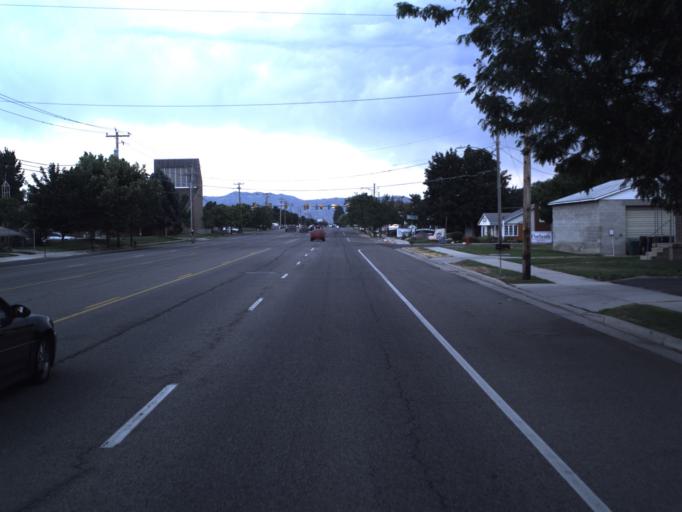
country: US
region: Utah
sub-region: Salt Lake County
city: Sandy City
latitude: 40.5971
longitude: -111.8723
